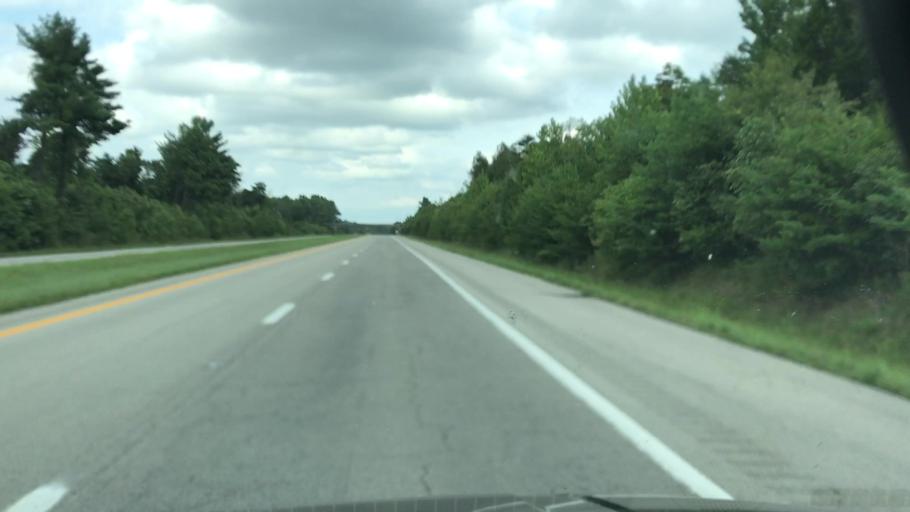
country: US
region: Kentucky
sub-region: Caldwell County
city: Princeton
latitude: 37.1445
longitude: -87.8034
